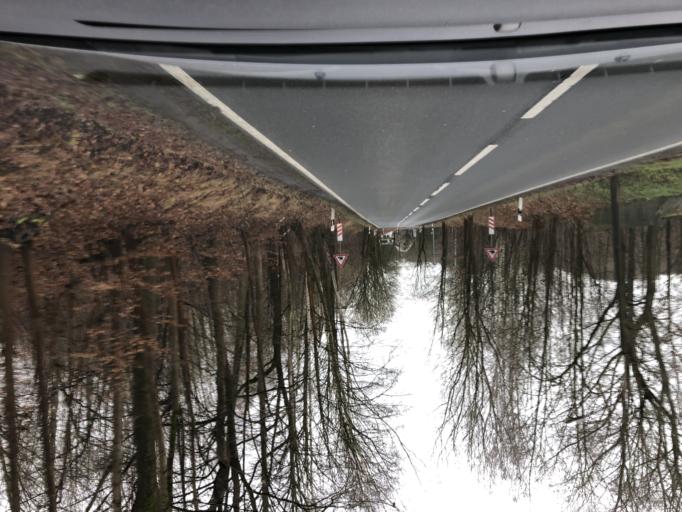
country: DE
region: Saxony
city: Niederstriegis
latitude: 51.0750
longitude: 13.1520
